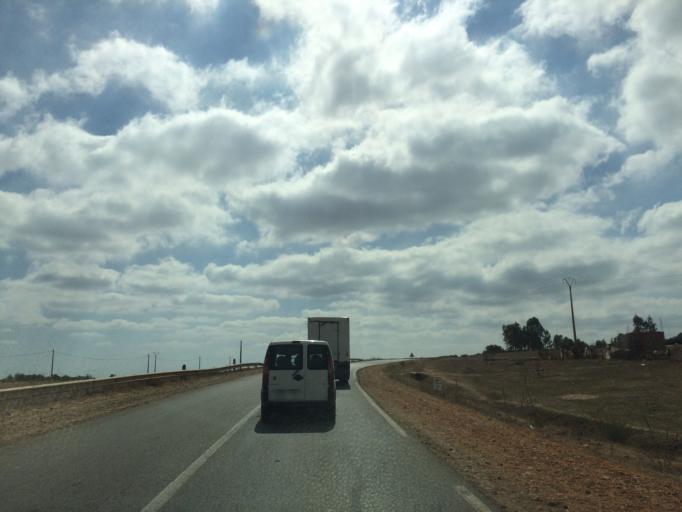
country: MA
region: Gharb-Chrarda-Beni Hssen
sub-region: Kenitra Province
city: Lalla Mimouna
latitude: 34.7740
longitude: -6.0802
